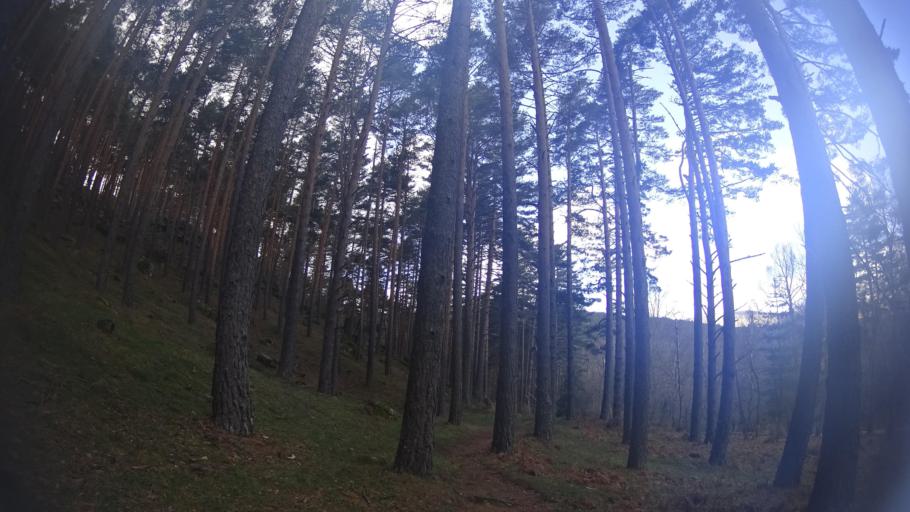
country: ES
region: Madrid
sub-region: Provincia de Madrid
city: Canencia
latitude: 40.8753
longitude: -3.7749
